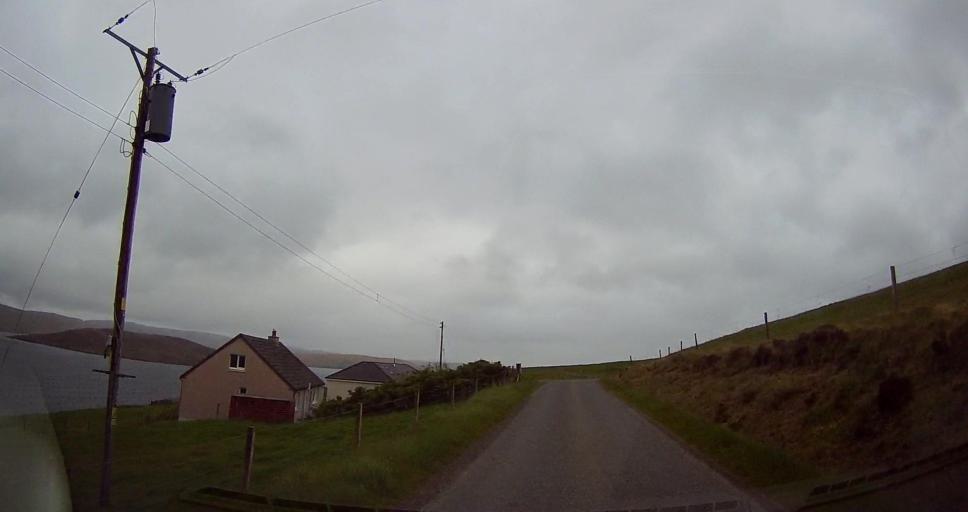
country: GB
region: Scotland
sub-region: Shetland Islands
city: Lerwick
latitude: 60.3701
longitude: -1.3823
